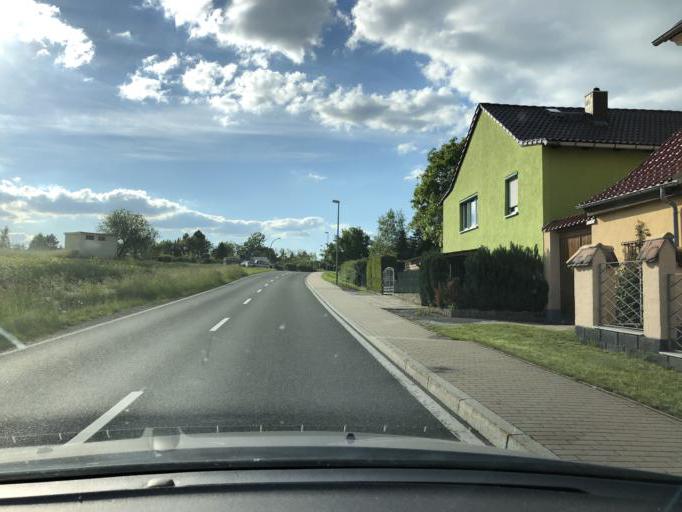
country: DE
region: Thuringia
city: Schmolln
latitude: 50.8915
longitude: 12.3666
